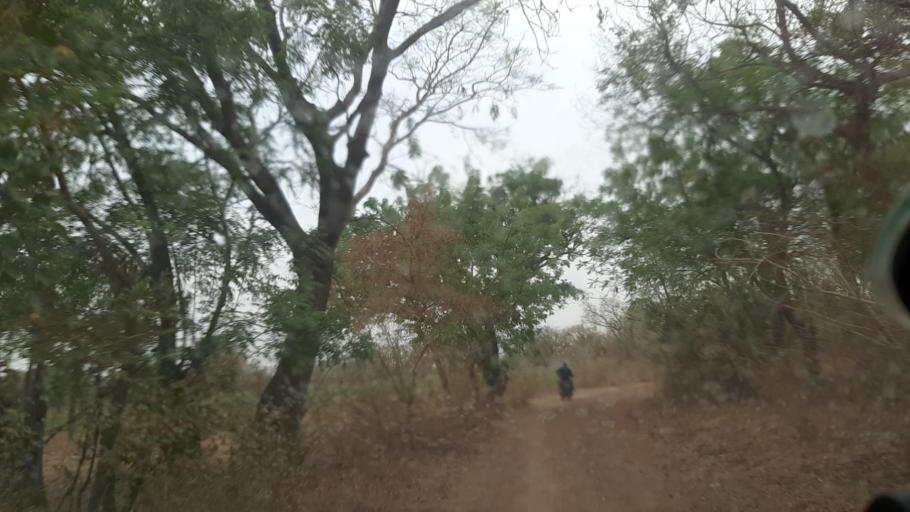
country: BF
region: Boucle du Mouhoun
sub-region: Province des Banwa
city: Salanso
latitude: 11.8490
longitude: -4.4221
